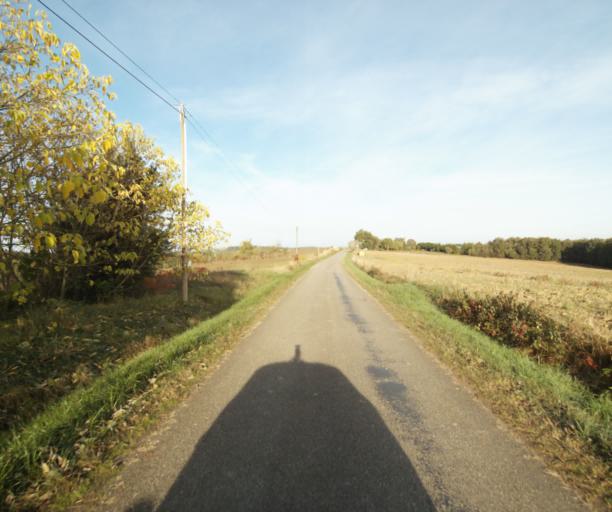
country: FR
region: Midi-Pyrenees
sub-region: Departement de la Haute-Garonne
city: Villemur-sur-Tarn
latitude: 43.9087
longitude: 1.4822
